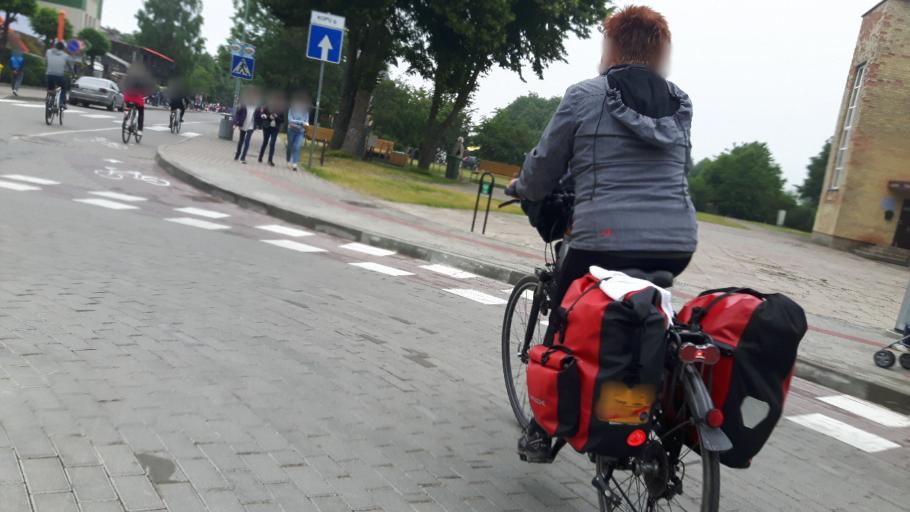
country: LT
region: Klaipedos apskritis
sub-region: Palanga
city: Sventoji
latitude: 56.0298
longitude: 21.0813
